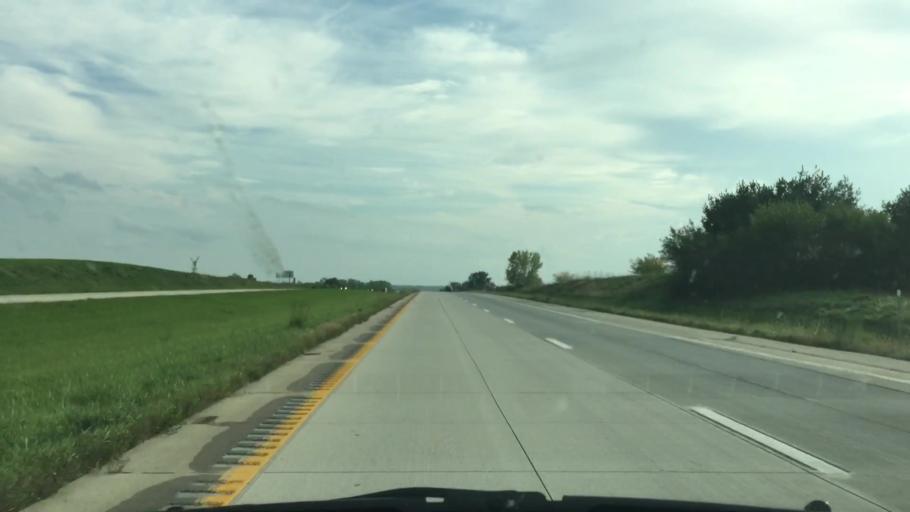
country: US
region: Missouri
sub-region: Daviess County
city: Gallatin
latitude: 40.0721
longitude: -94.0938
